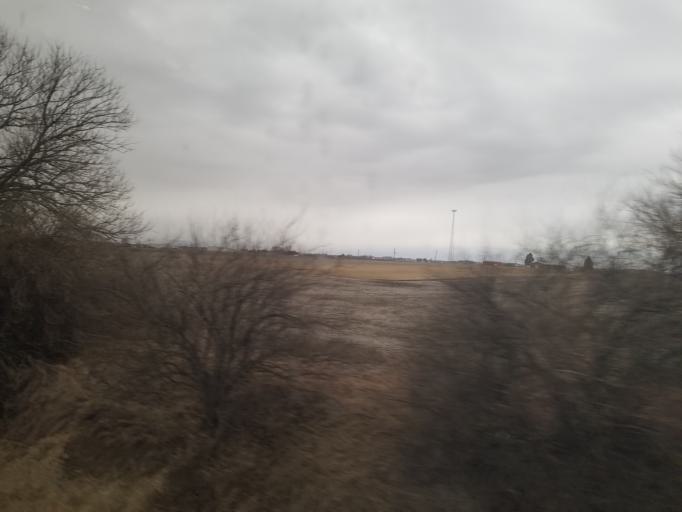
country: US
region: Illinois
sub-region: LaSalle County
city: Mendota
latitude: 41.5658
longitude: -89.0585
